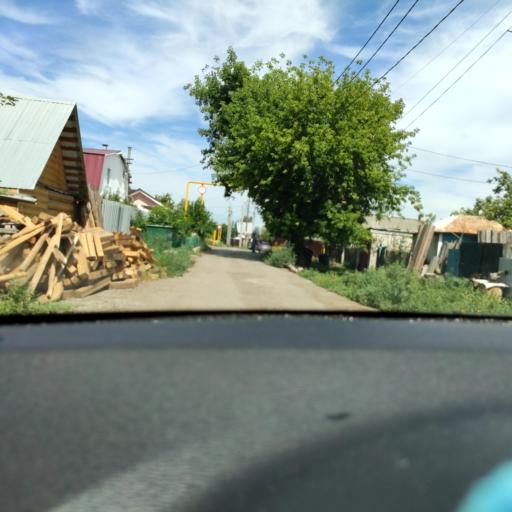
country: RU
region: Samara
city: Smyshlyayevka
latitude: 53.2390
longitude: 50.3416
